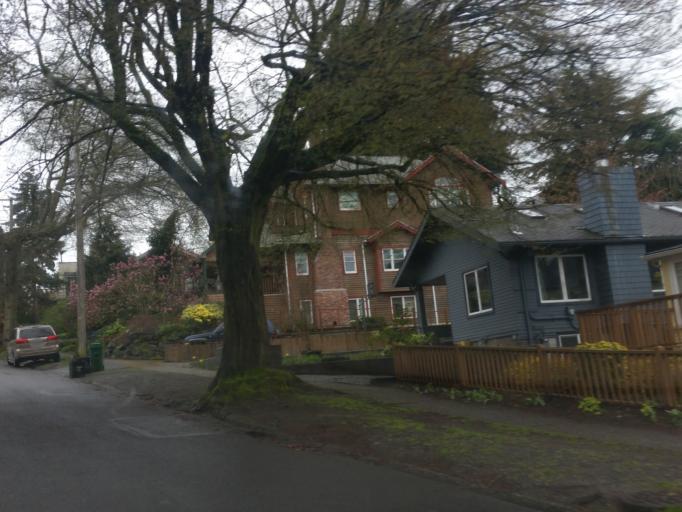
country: US
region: Washington
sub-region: King County
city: Seattle
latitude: 47.6703
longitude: -122.3566
